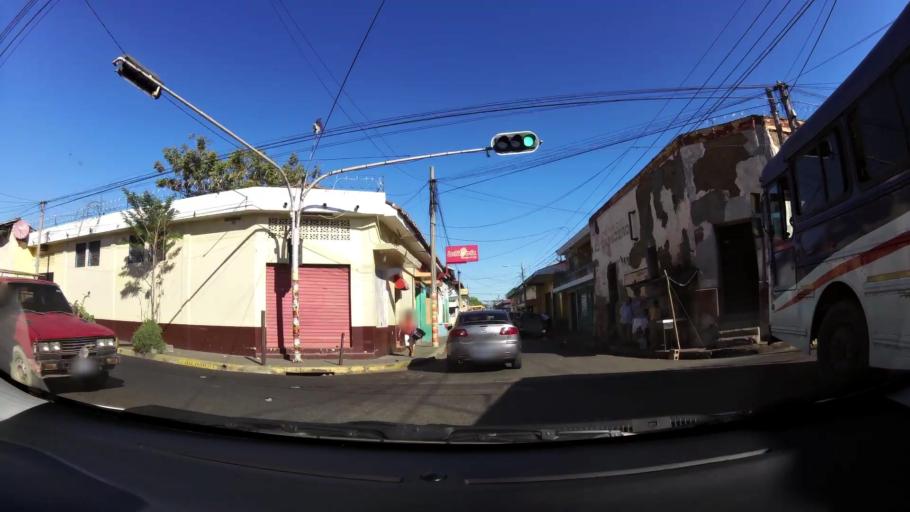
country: SV
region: San Miguel
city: San Miguel
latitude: 13.4786
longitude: -88.1783
